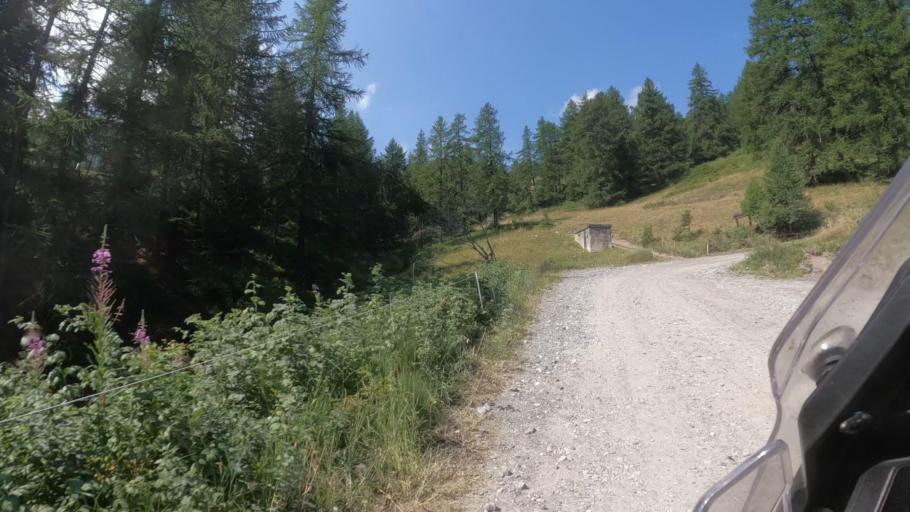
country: IT
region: Piedmont
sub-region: Provincia di Torino
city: Cesana Torinese
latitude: 44.9211
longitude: 6.8080
